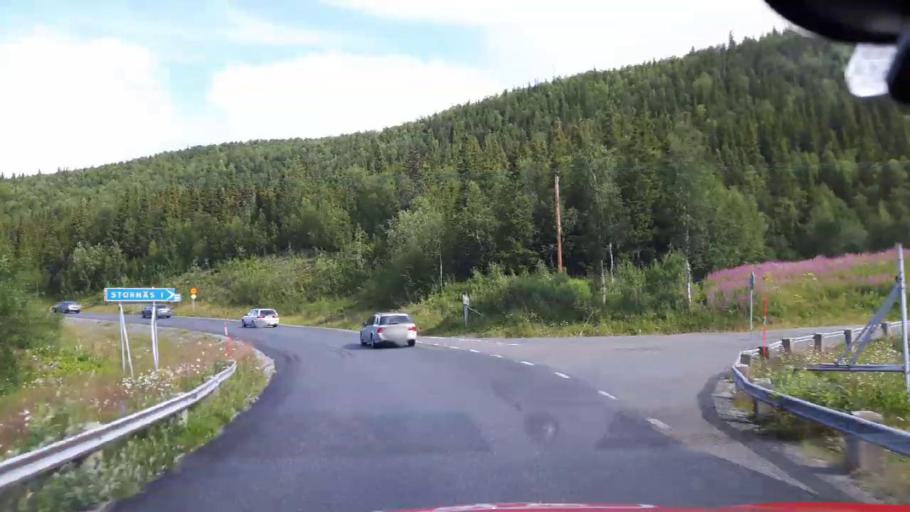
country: SE
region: Vaesterbotten
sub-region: Vilhelmina Kommun
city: Sjoberg
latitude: 65.0323
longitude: 15.1404
